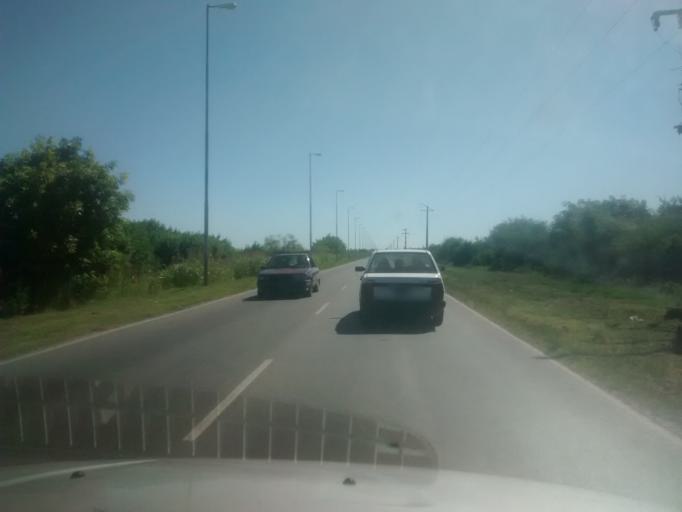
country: AR
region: Buenos Aires
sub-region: Partido de Berisso
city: Berisso
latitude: -34.8935
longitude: -57.8769
